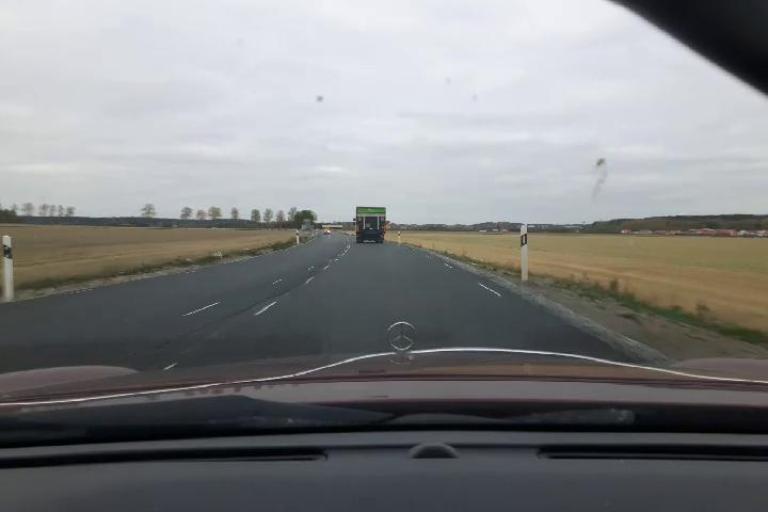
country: SE
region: Uppsala
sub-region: Enkopings Kommun
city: Enkoping
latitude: 59.6193
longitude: 17.0414
